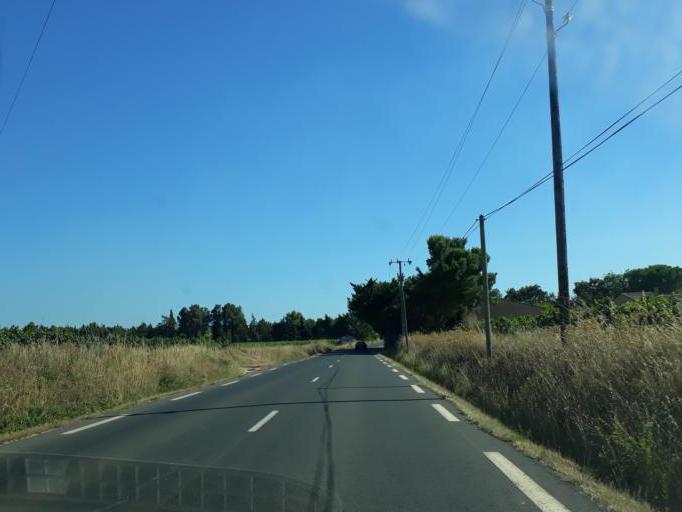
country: FR
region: Languedoc-Roussillon
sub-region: Departement de l'Herault
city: Agde
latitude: 43.3360
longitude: 3.4832
